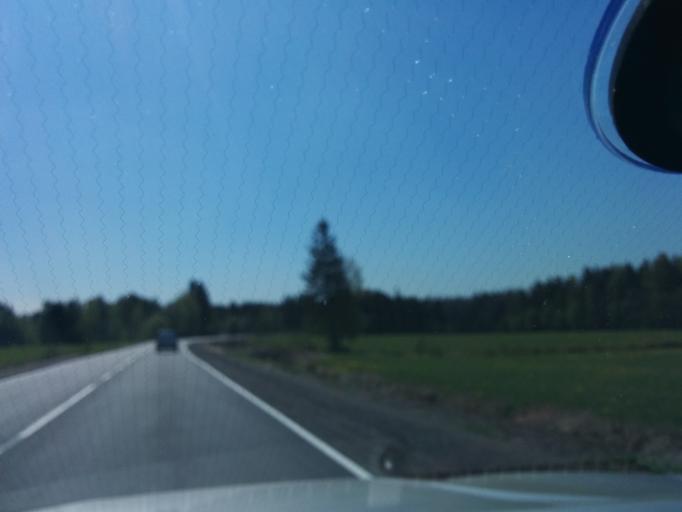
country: RU
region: Leningrad
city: Verkhniye Osel'ki
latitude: 60.2019
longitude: 30.4262
